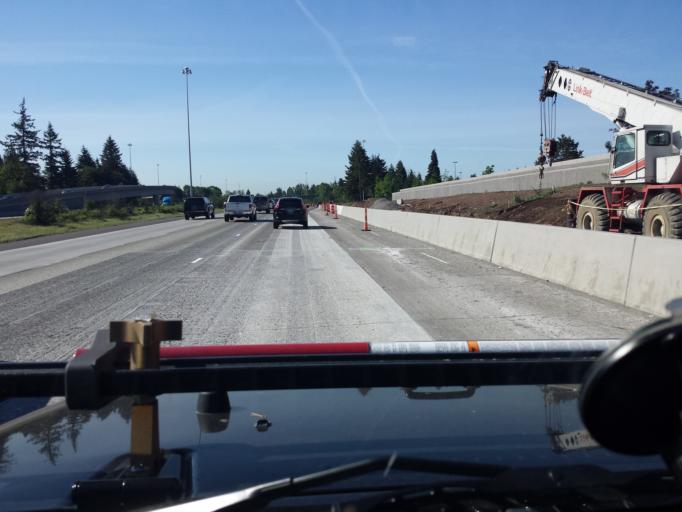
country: US
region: Washington
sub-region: Clark County
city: Orchards
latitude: 45.6267
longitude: -122.5598
